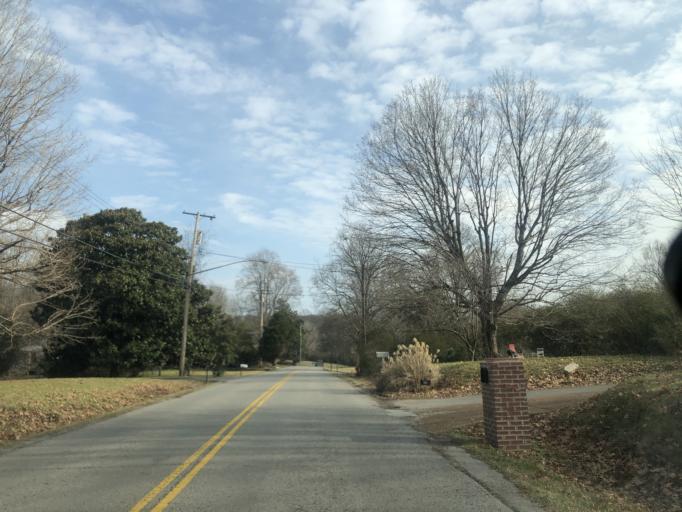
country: US
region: Tennessee
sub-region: Davidson County
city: Oak Hill
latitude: 36.1183
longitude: -86.7153
